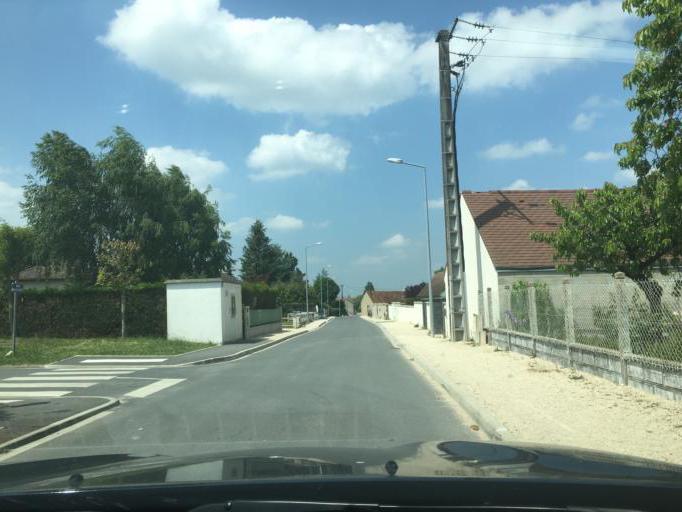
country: FR
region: Centre
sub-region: Departement du Loiret
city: Trainou
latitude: 47.9791
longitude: 2.1068
